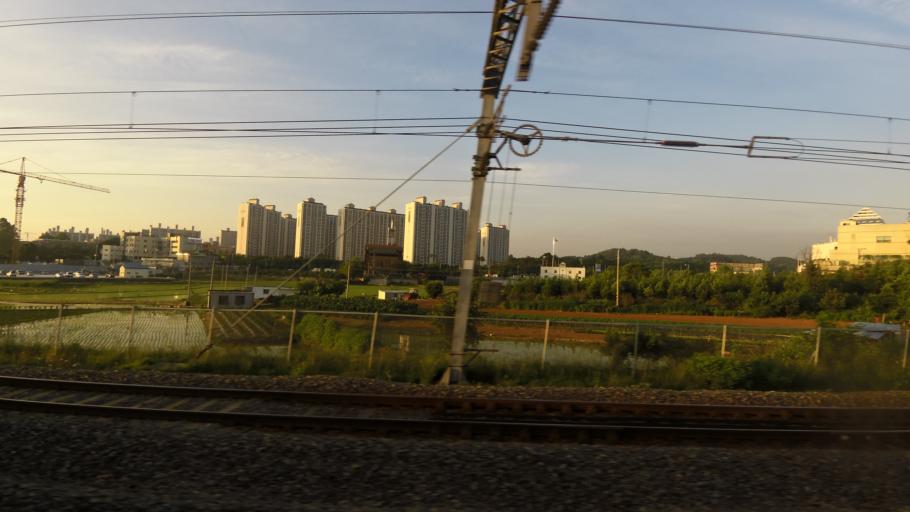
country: KR
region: Gyeonggi-do
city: Osan
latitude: 37.0448
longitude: 127.0569
